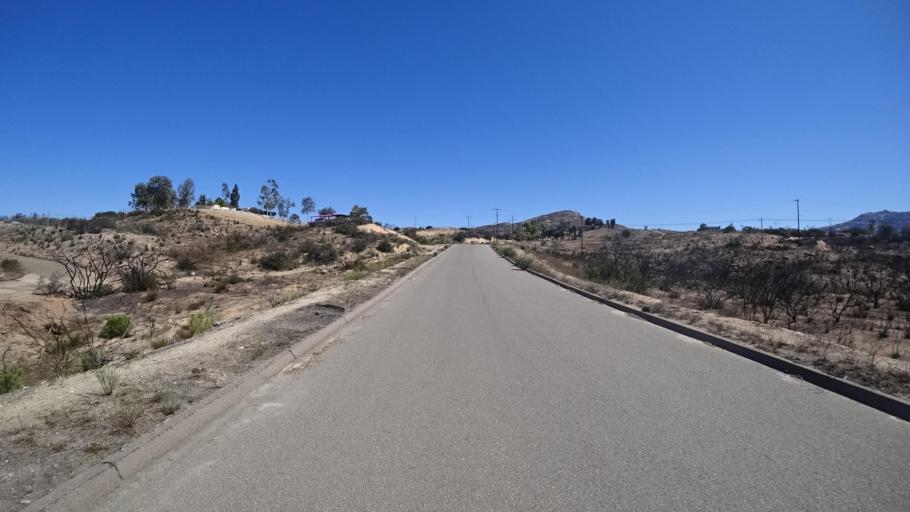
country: US
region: California
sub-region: San Diego County
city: Alpine
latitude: 32.7656
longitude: -116.7676
